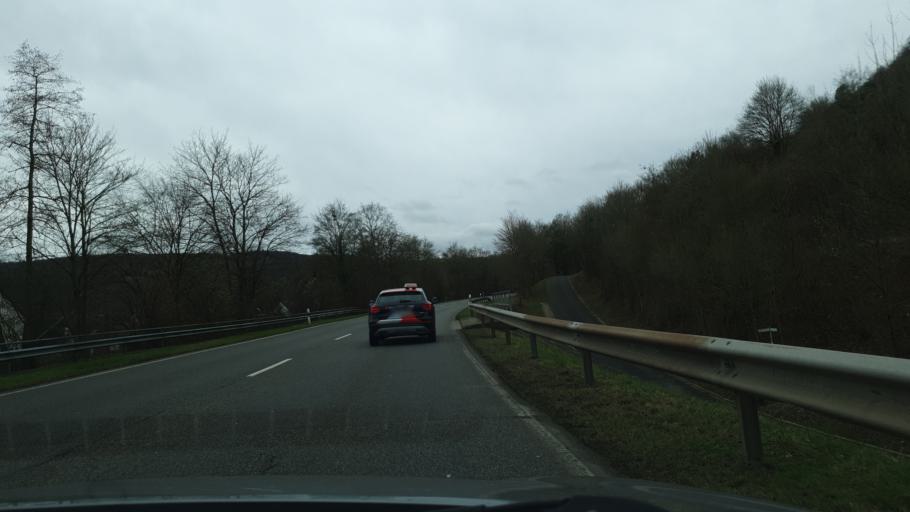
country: DE
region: Rheinland-Pfalz
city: Spay
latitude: 50.2530
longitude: 7.6429
